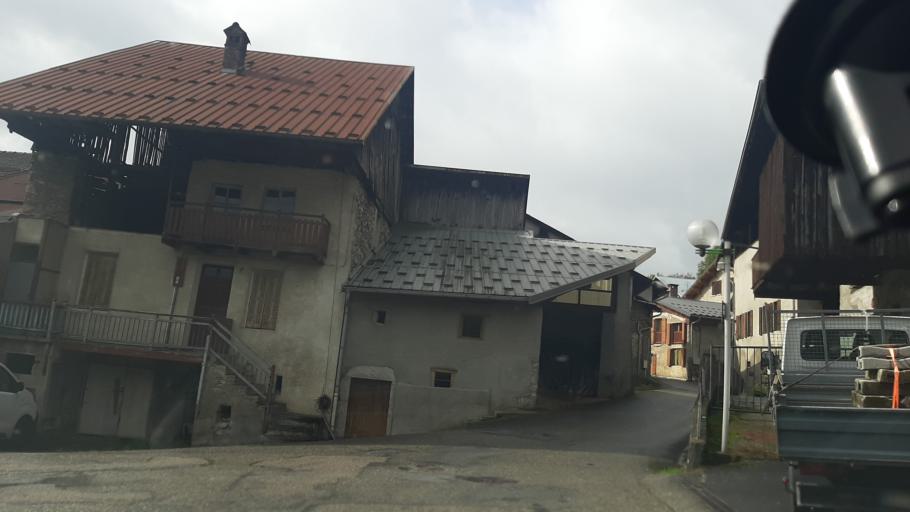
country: FR
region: Rhone-Alpes
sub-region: Departement de la Savoie
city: Gresy-sur-Isere
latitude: 45.6117
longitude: 6.2671
